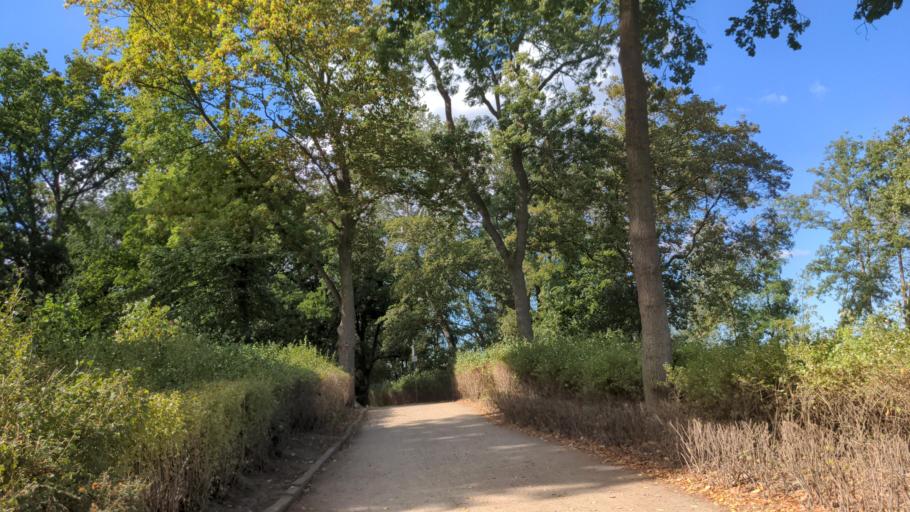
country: DE
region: Mecklenburg-Vorpommern
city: Wismar
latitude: 53.9118
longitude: 11.4296
